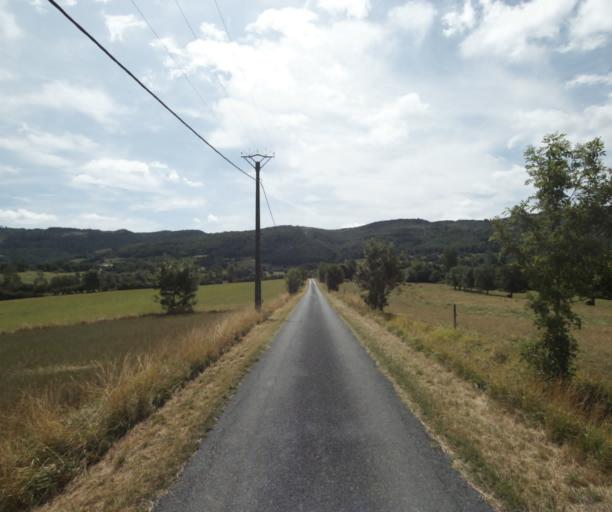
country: FR
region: Midi-Pyrenees
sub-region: Departement du Tarn
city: Dourgne
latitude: 43.4746
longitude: 2.1139
